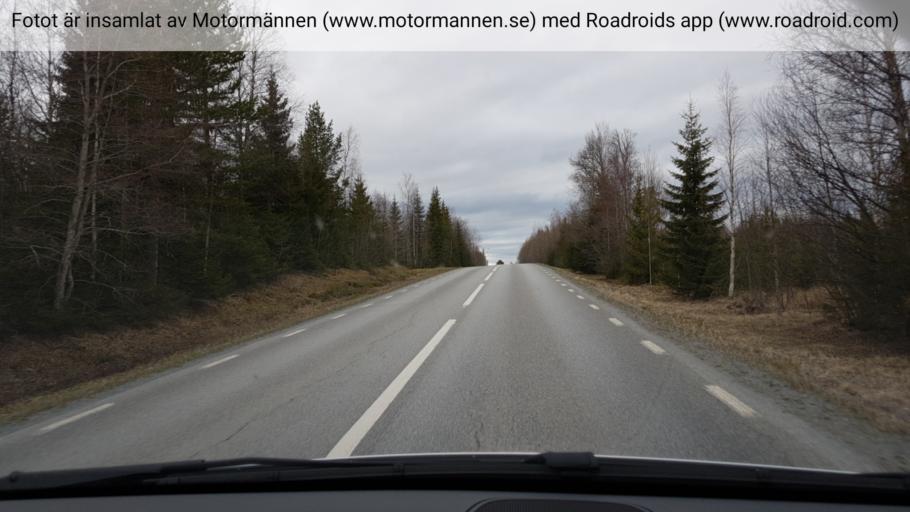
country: SE
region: Jaemtland
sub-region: Krokoms Kommun
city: Krokom
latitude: 63.1581
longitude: 14.1387
